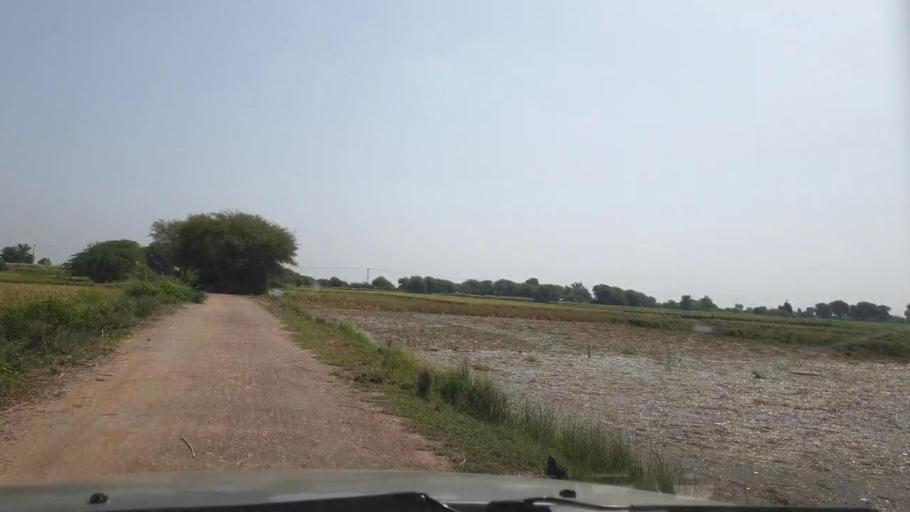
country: PK
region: Sindh
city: Tando Ghulam Ali
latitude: 25.0948
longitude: 68.7683
